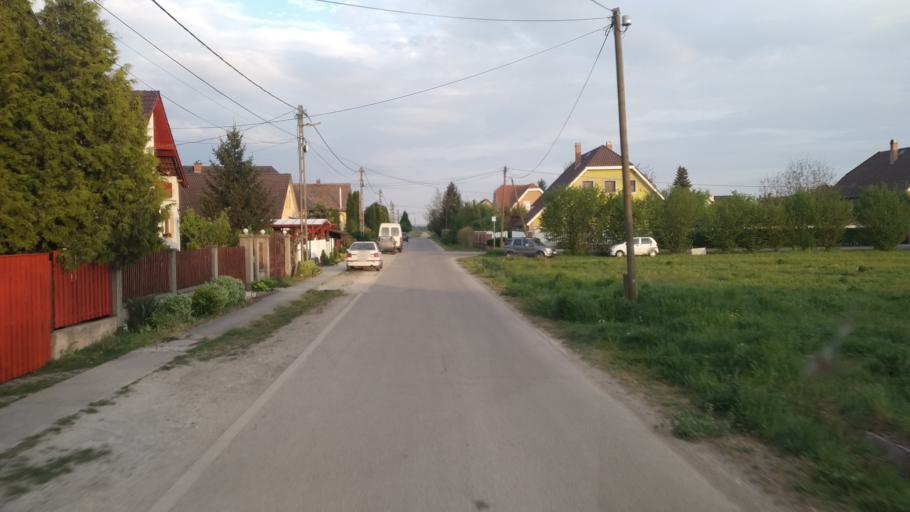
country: HU
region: Pest
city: Tahitotfalu
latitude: 47.7521
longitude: 19.0997
